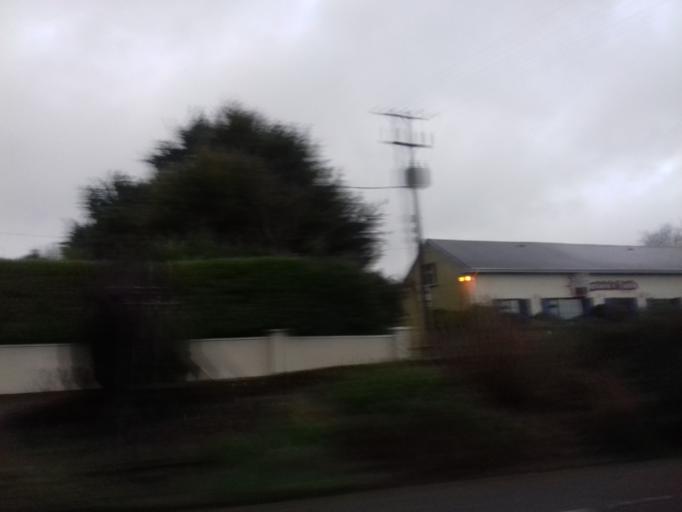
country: IE
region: Munster
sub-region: Ciarrai
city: Castleisland
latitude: 52.2943
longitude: -9.3932
